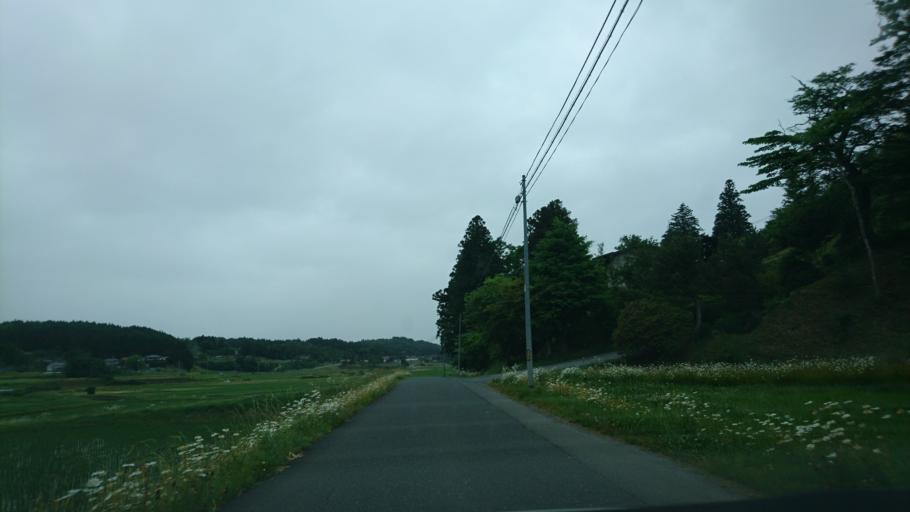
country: JP
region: Iwate
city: Ichinoseki
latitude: 38.9174
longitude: 141.1783
